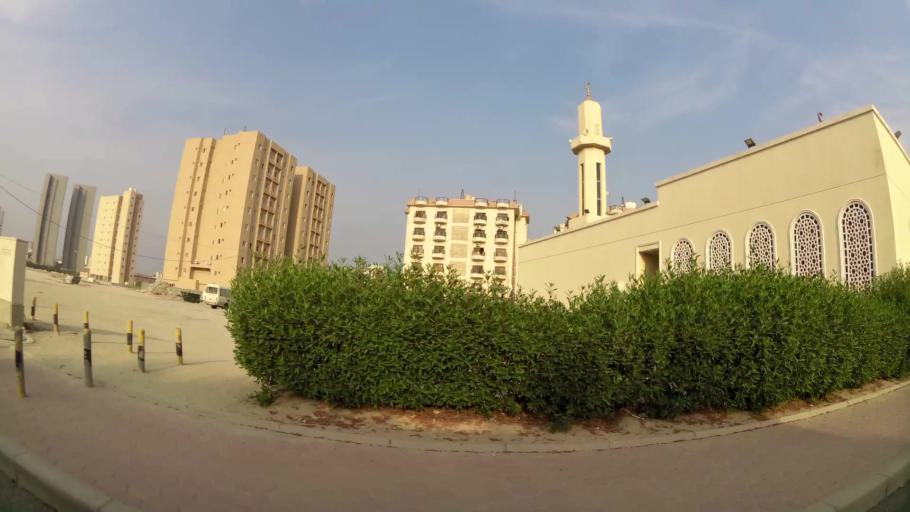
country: KW
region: Mubarak al Kabir
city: Sabah as Salim
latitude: 29.2527
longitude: 48.0796
